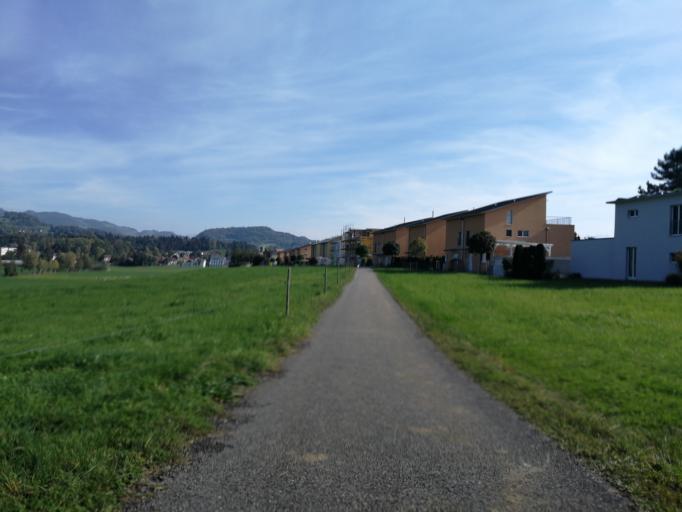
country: CH
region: Zurich
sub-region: Bezirk Hinwil
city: Durnten
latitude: 47.2699
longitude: 8.8404
